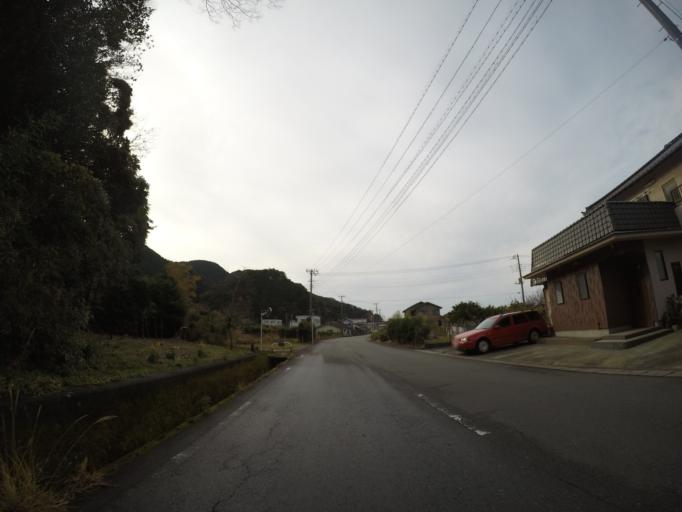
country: JP
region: Shizuoka
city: Heda
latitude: 34.8468
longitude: 138.7794
